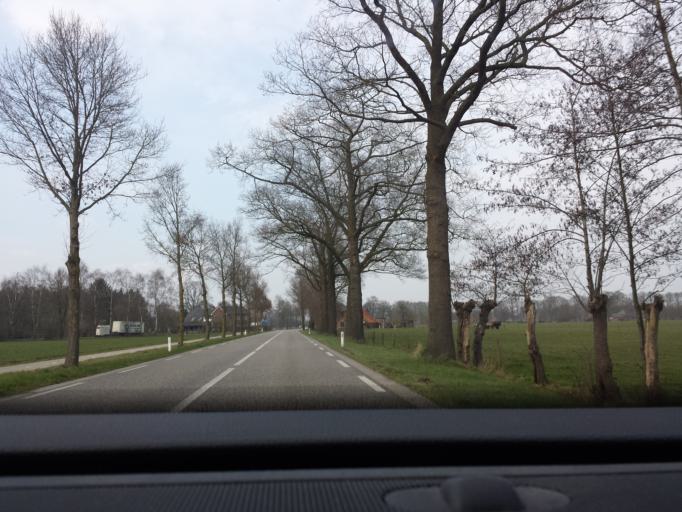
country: NL
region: Gelderland
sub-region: Oude IJsselstreek
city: Varsseveld
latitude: 51.9798
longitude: 6.4391
